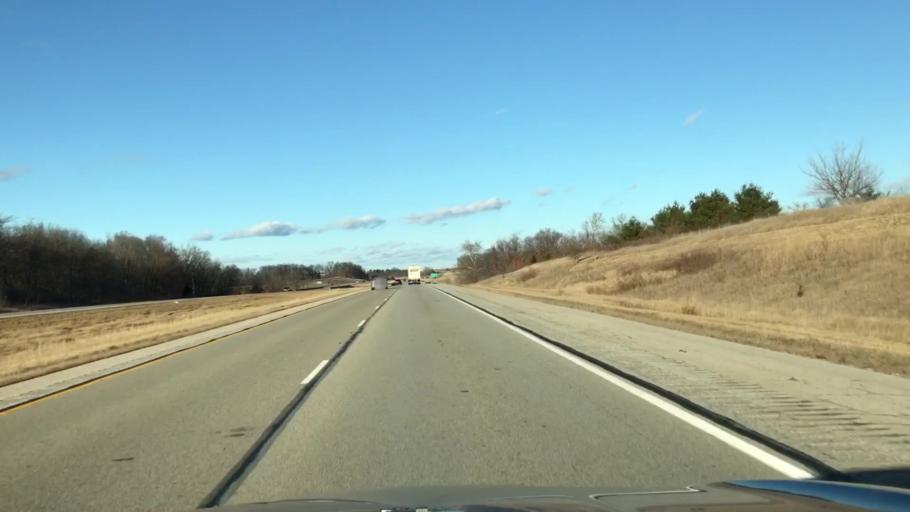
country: US
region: Illinois
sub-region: McLean County
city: Lexington
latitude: 40.6270
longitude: -88.8169
